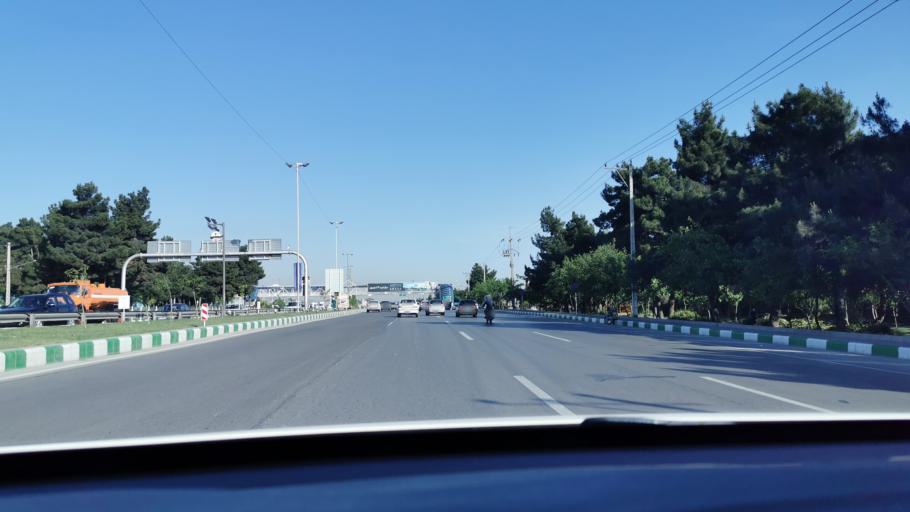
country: IR
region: Razavi Khorasan
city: Mashhad
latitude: 36.2529
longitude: 59.6055
